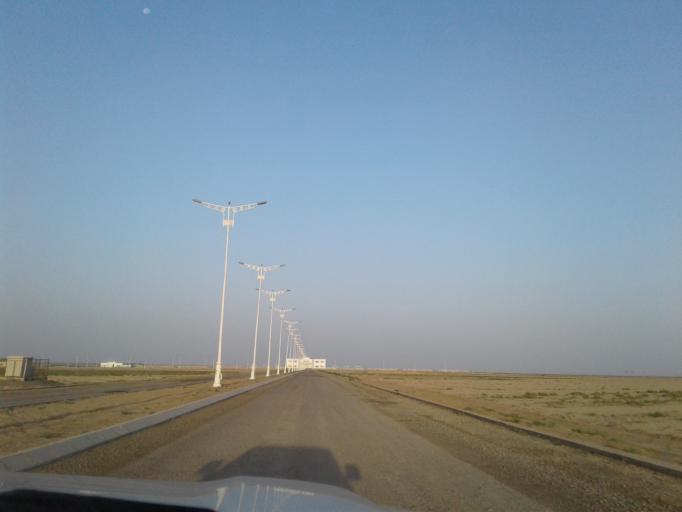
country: IR
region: Golestan
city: Aq Qayeh
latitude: 37.7062
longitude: 54.7510
